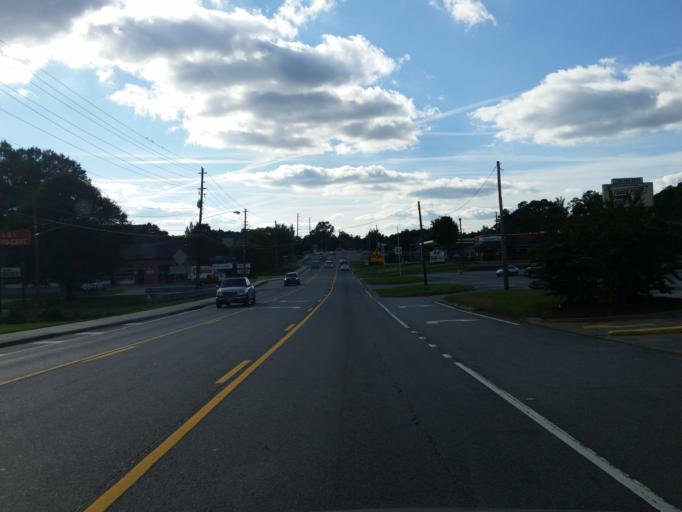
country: US
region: Georgia
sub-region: Cobb County
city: Marietta
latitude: 33.9519
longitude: -84.5711
